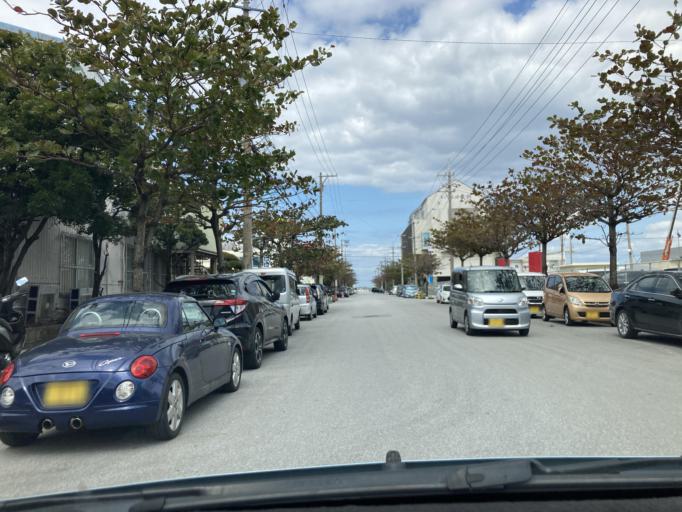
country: JP
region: Okinawa
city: Naha-shi
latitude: 26.2477
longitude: 127.6732
